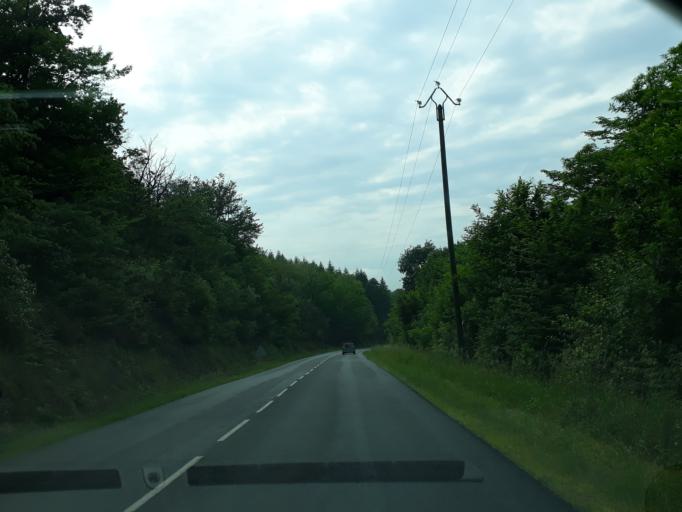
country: FR
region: Limousin
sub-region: Departement de la Correze
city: Beynat
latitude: 45.1232
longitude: 1.7160
